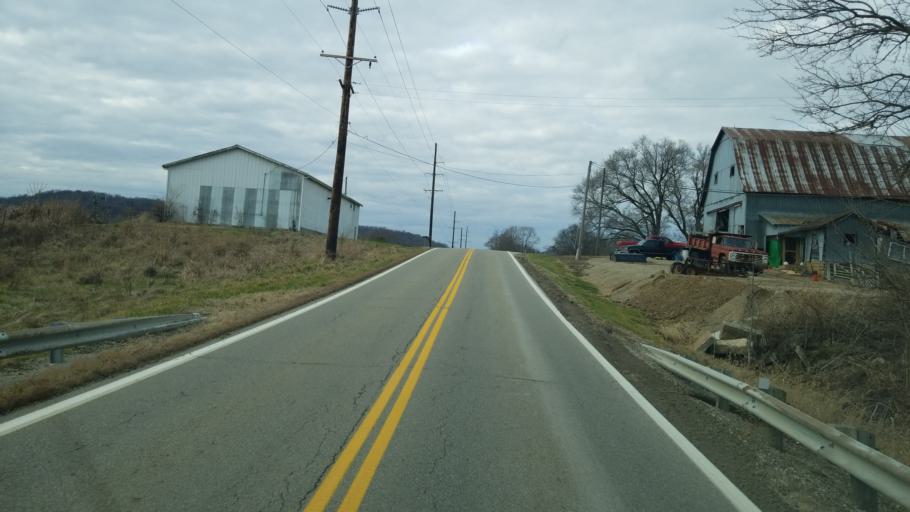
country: US
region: Ohio
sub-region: Ross County
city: Frankfort
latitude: 39.3482
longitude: -83.2082
